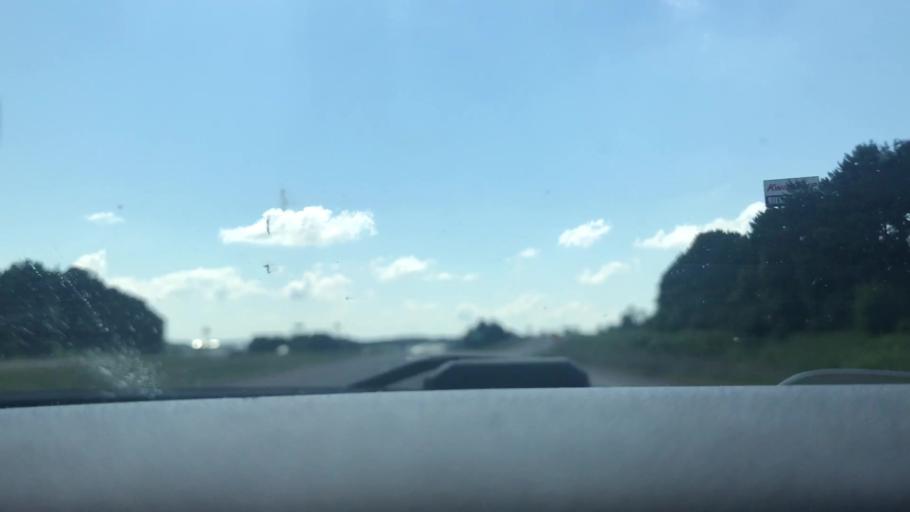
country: US
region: Wisconsin
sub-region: Chippewa County
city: Bloomer
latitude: 45.1027
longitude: -91.5089
